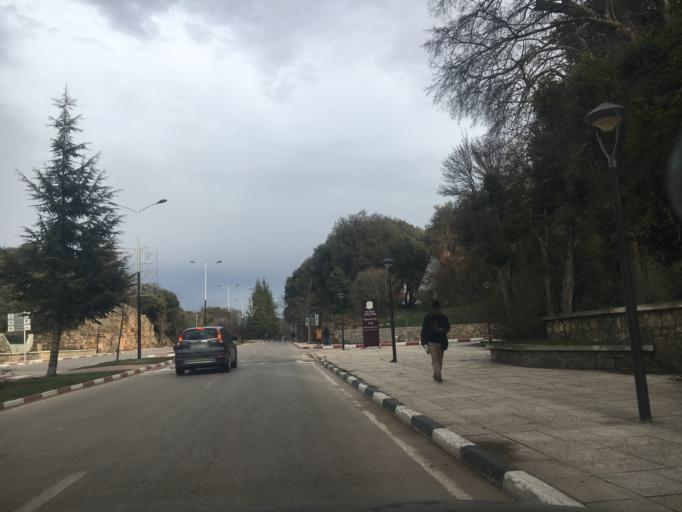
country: MA
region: Meknes-Tafilalet
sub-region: Ifrane
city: Ifrane
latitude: 33.5273
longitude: -5.1190
